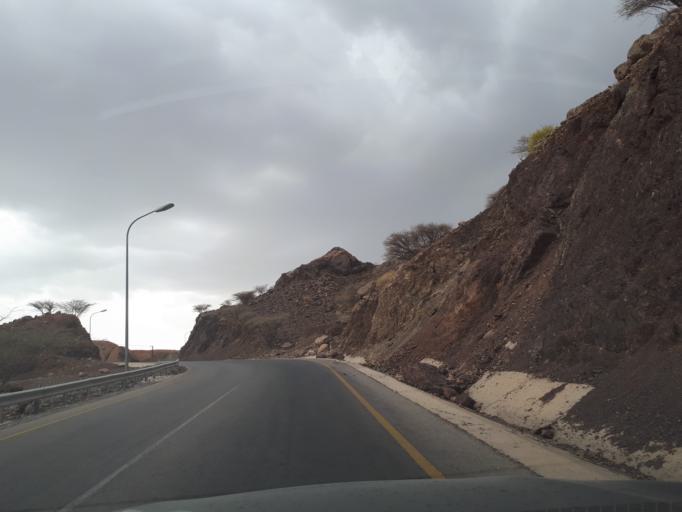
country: OM
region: Ash Sharqiyah
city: Badiyah
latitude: 22.5698
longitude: 59.0800
